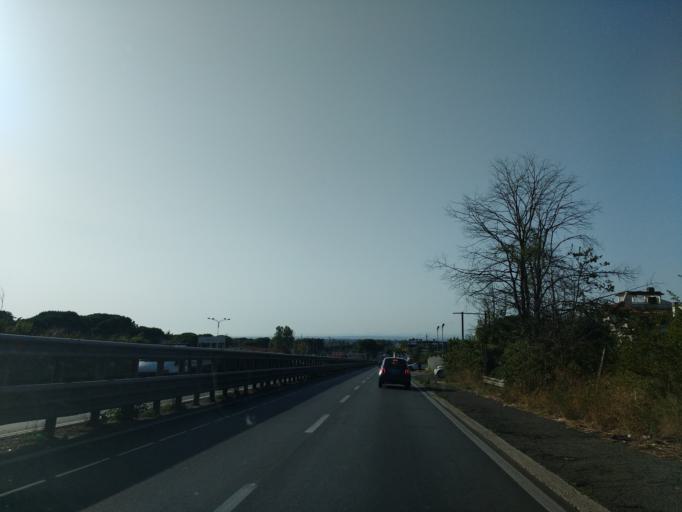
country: IT
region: Latium
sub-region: Citta metropolitana di Roma Capitale
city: Marino
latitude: 41.7705
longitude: 12.6132
